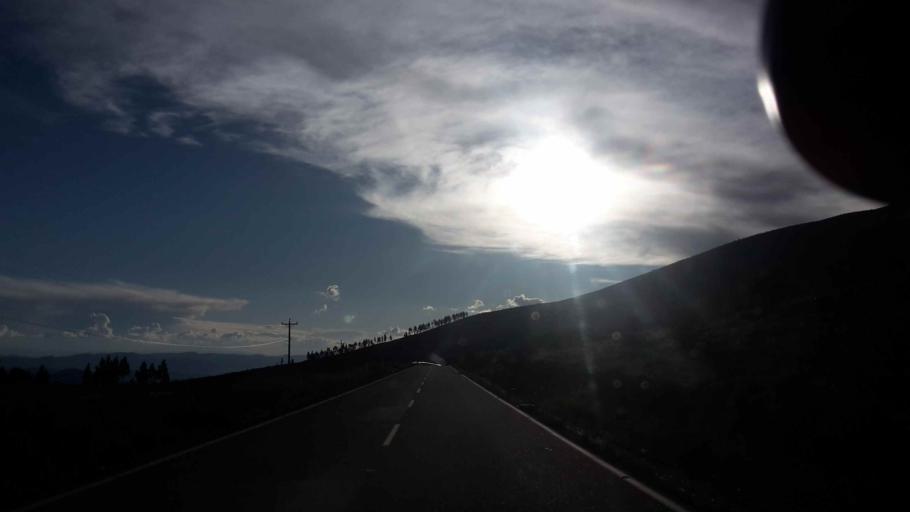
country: BO
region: Cochabamba
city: Arani
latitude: -17.5604
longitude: -65.7079
